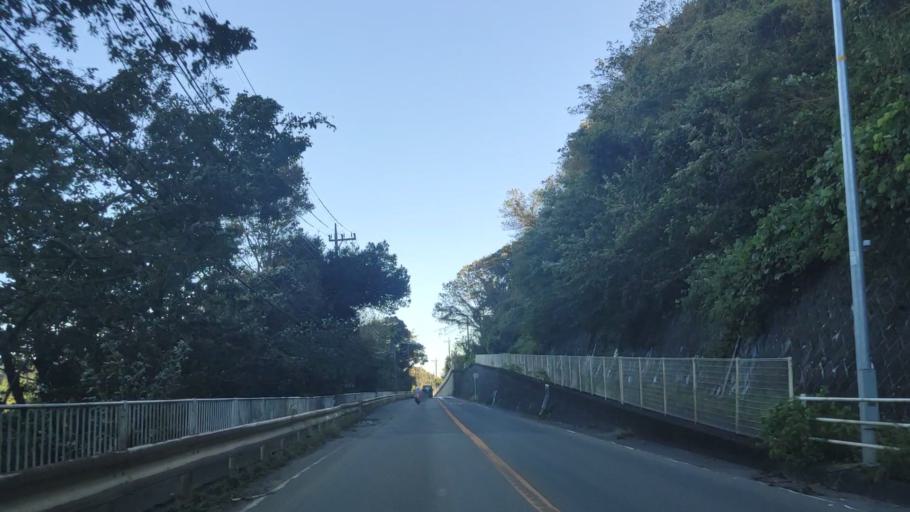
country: JP
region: Tokyo
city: Hachioji
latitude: 35.5624
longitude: 139.3168
